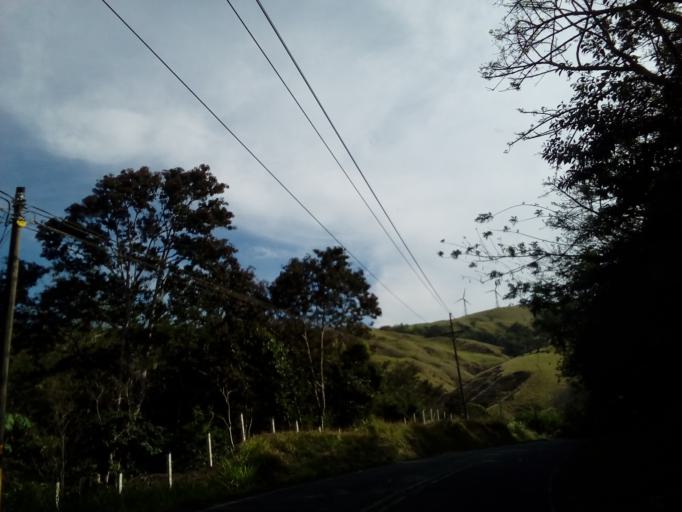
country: CR
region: Guanacaste
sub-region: Canton de Tilaran
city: Tilaran
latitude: 10.5274
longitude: -84.9709
